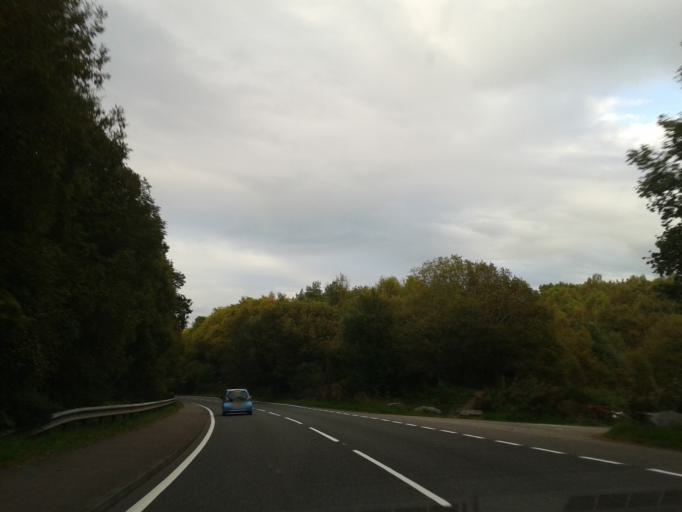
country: GB
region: Scotland
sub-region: Highland
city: Inverness
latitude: 57.4600
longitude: -4.2591
